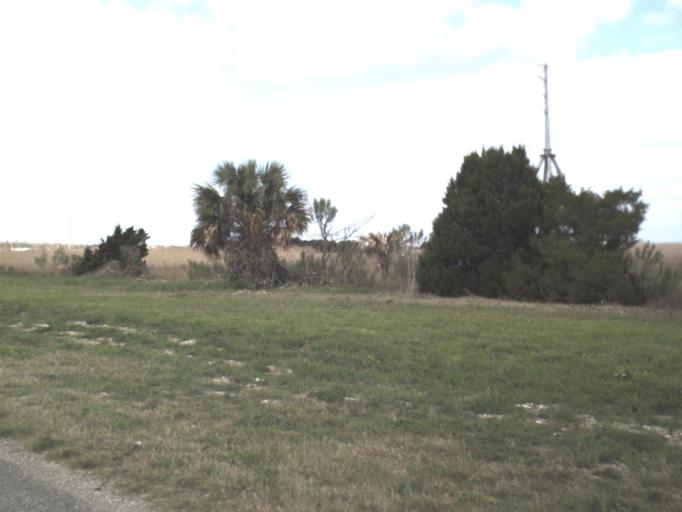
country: US
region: Florida
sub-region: Franklin County
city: Apalachicola
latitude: 29.7263
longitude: -84.9695
